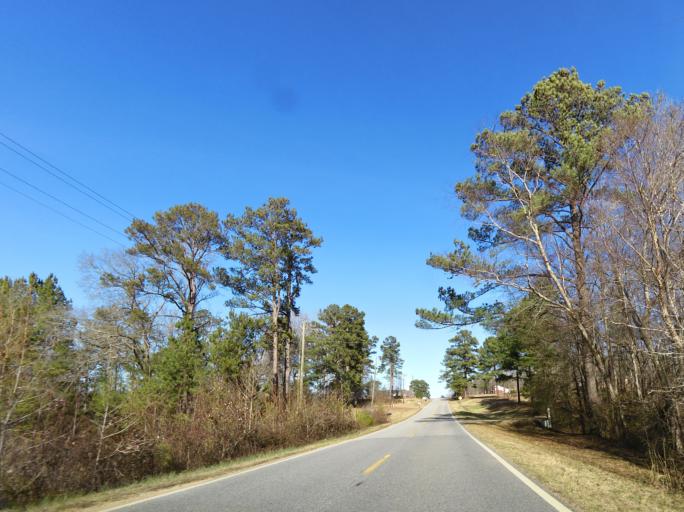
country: US
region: Georgia
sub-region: Bibb County
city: West Point
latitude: 32.7622
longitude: -83.8766
